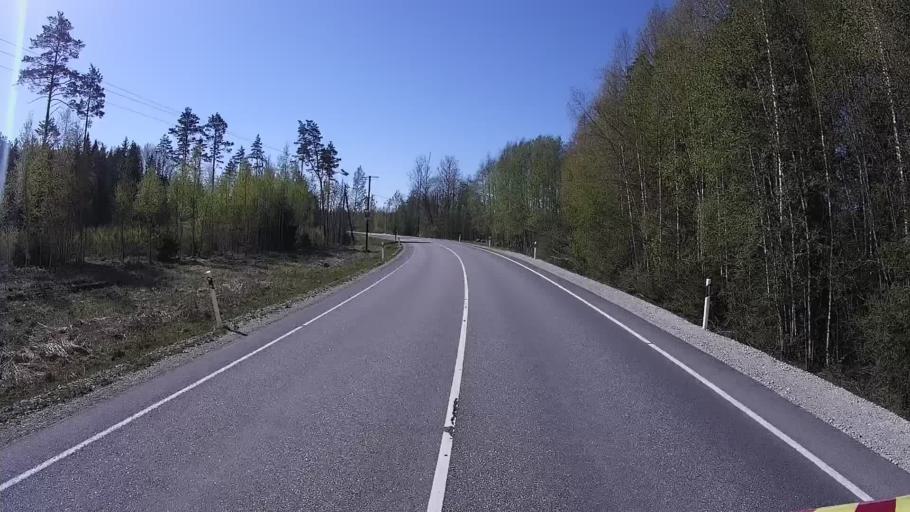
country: EE
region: Raplamaa
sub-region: Jaervakandi vald
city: Jarvakandi
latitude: 58.7583
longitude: 24.8136
